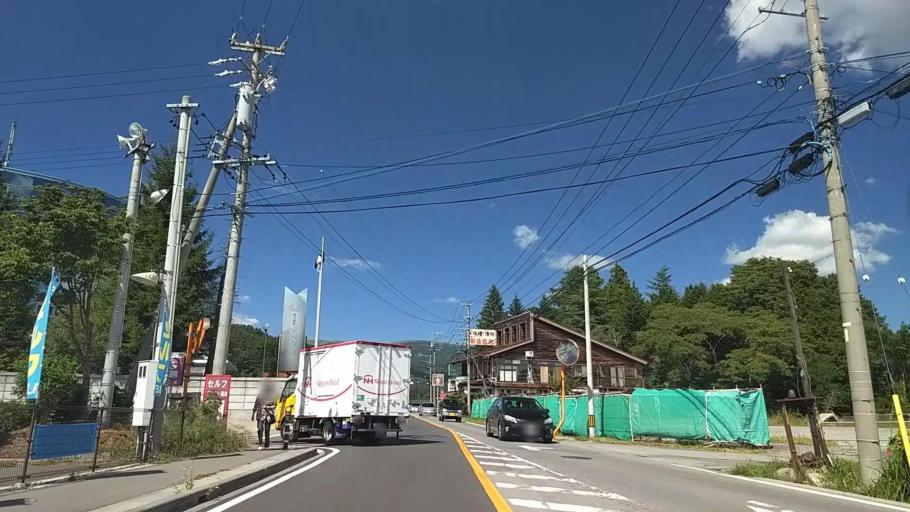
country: JP
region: Nagano
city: Chino
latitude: 36.0127
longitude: 138.1756
